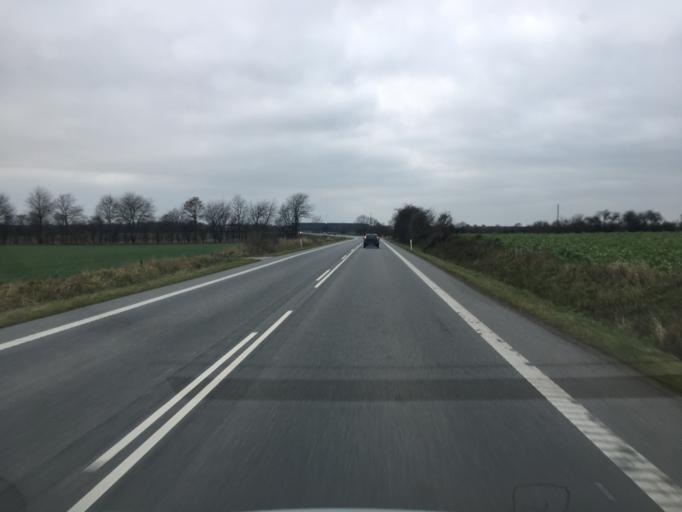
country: DK
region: South Denmark
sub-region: Aabenraa Kommune
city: Rodekro
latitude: 55.0266
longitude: 9.3381
